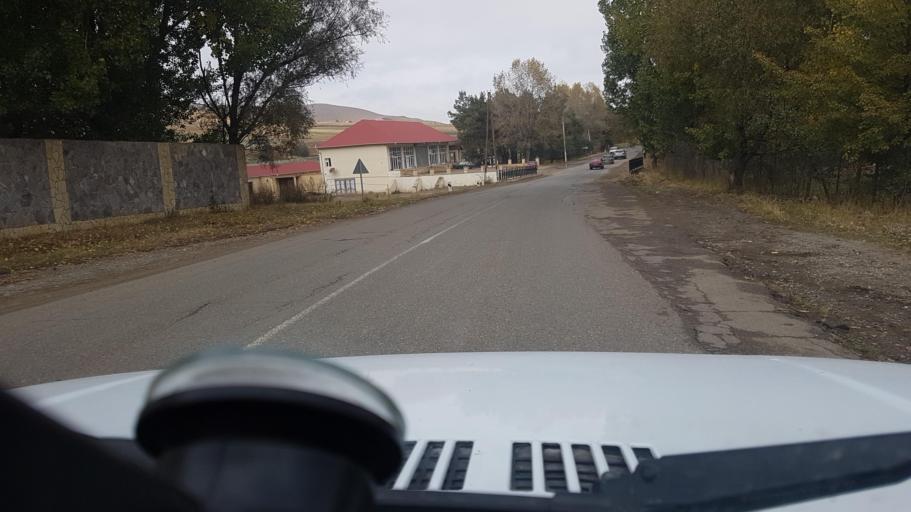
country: AZ
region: Gadabay Rayon
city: Ariqdam
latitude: 40.6334
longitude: 45.8133
